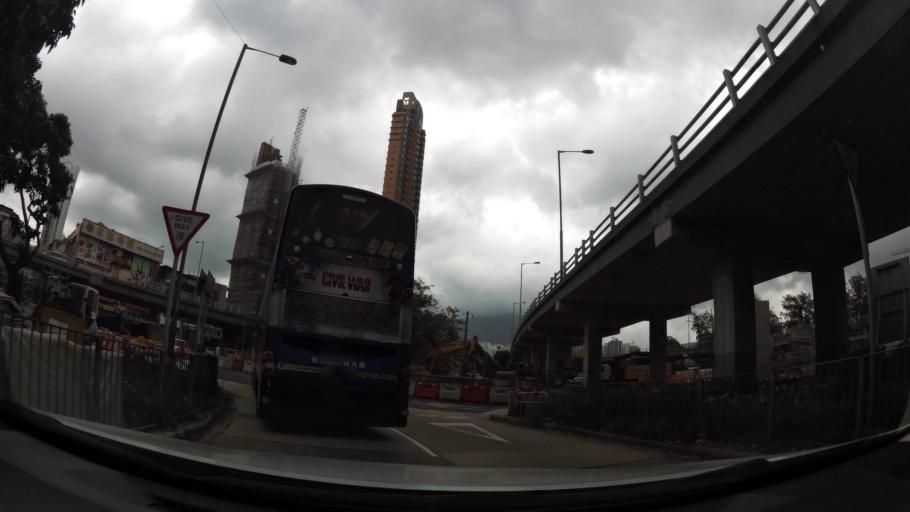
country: HK
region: Kowloon City
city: Kowloon
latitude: 22.3271
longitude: 114.1892
